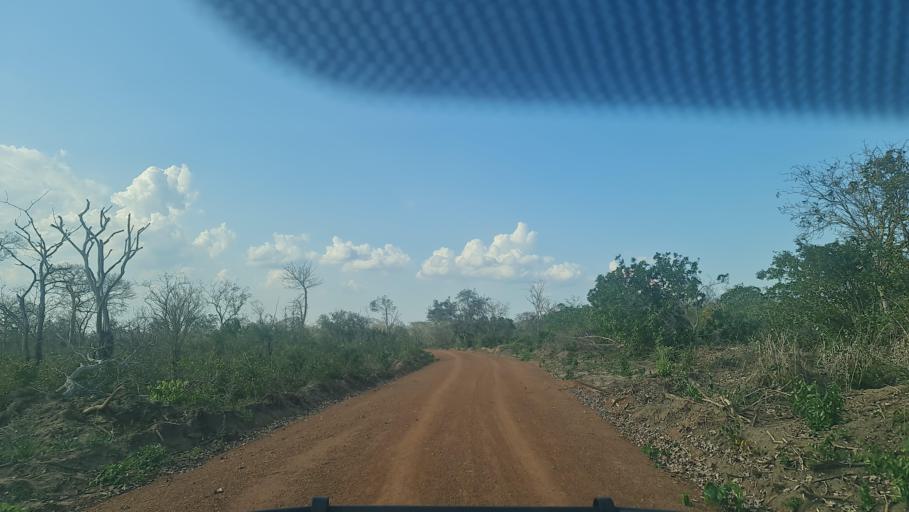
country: MZ
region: Nampula
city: Ilha de Mocambique
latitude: -15.5091
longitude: 40.1636
